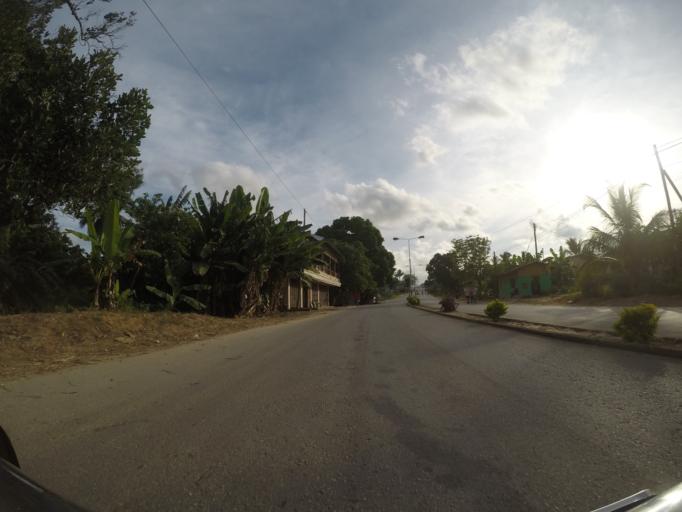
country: TZ
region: Pemba South
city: Chake Chake
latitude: -5.2569
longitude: 39.7755
